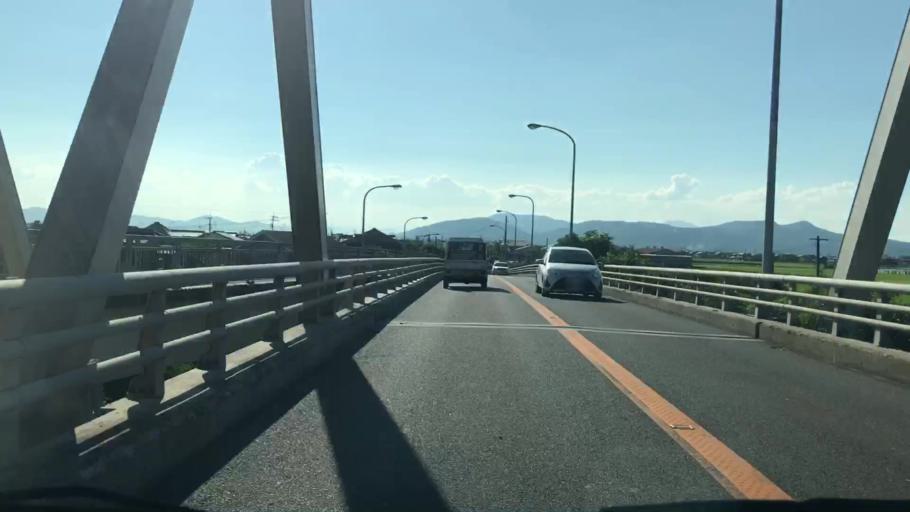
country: JP
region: Saga Prefecture
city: Saga-shi
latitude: 33.2197
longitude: 130.2513
